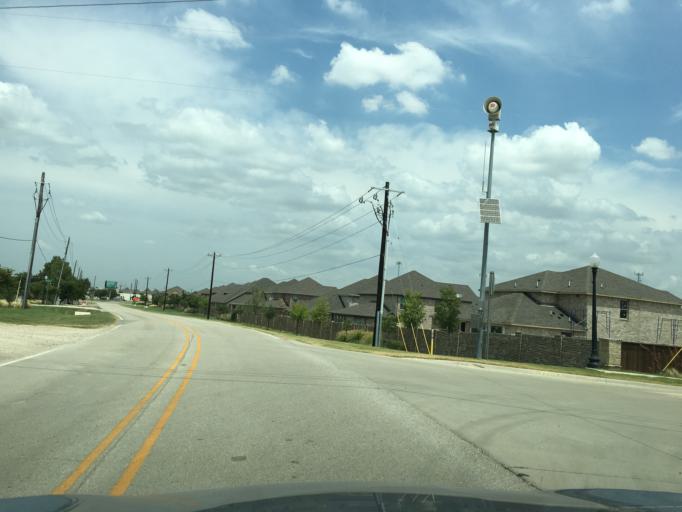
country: US
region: Texas
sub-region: Denton County
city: The Colony
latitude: 33.0419
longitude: -96.8619
